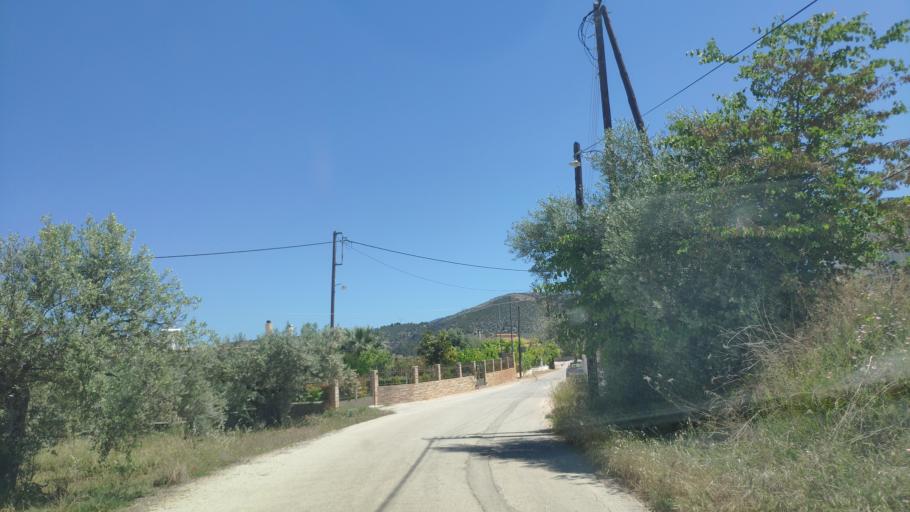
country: GR
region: Peloponnese
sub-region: Nomos Korinthias
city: Athikia
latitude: 37.8135
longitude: 22.9213
